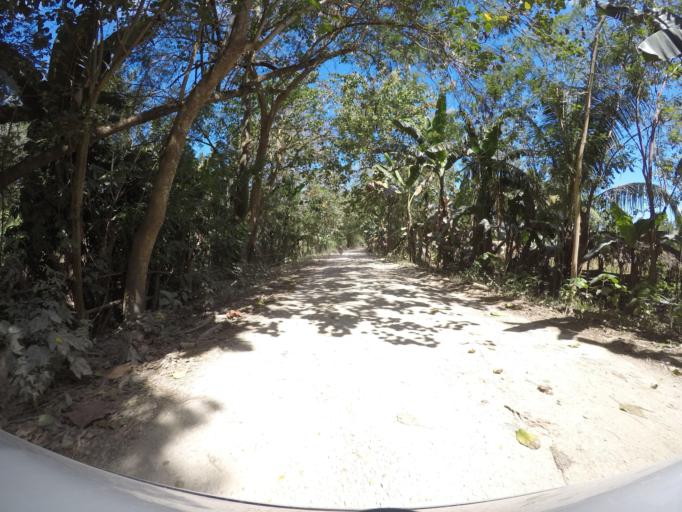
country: TL
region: Viqueque
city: Viqueque
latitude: -8.9335
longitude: 126.4122
